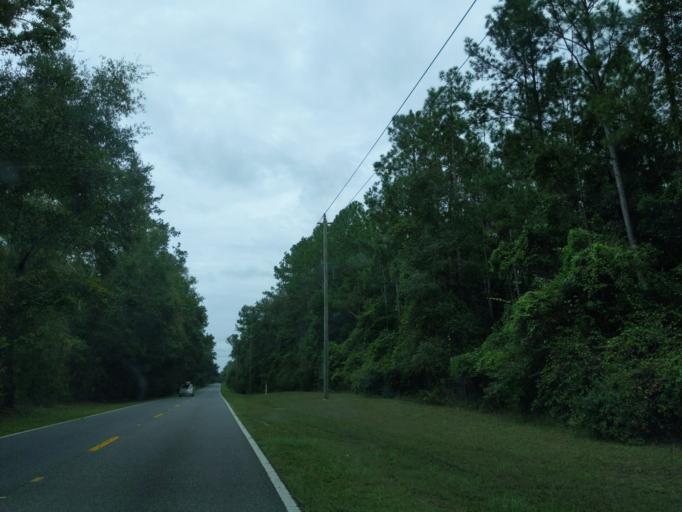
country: US
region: Florida
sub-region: Leon County
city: Woodville
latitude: 30.3679
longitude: -84.1658
